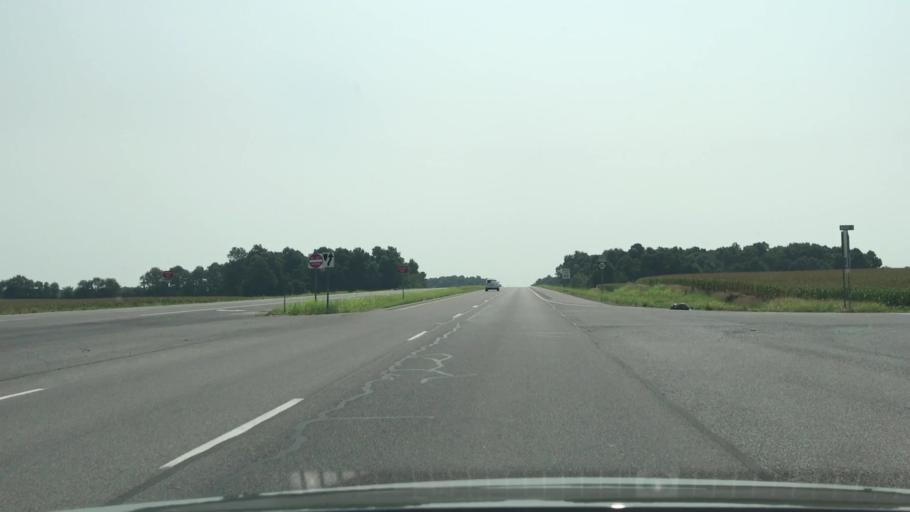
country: US
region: Kentucky
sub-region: Graves County
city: Mayfield
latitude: 36.6777
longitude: -88.5242
